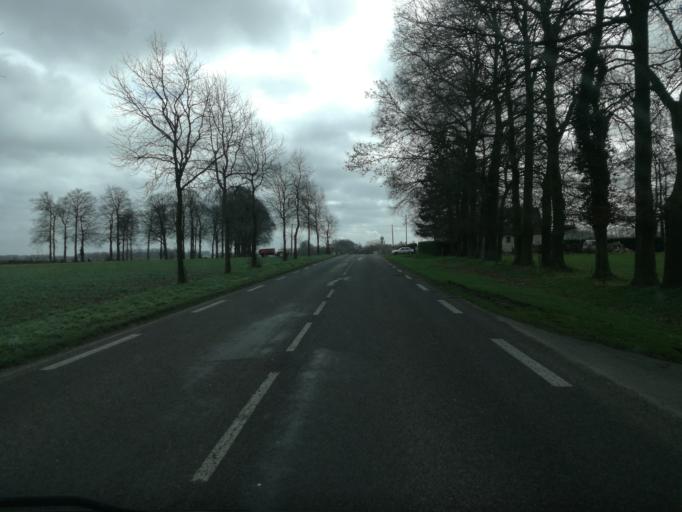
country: FR
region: Haute-Normandie
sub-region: Departement de la Seine-Maritime
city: Valliquerville
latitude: 49.6190
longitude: 0.6561
